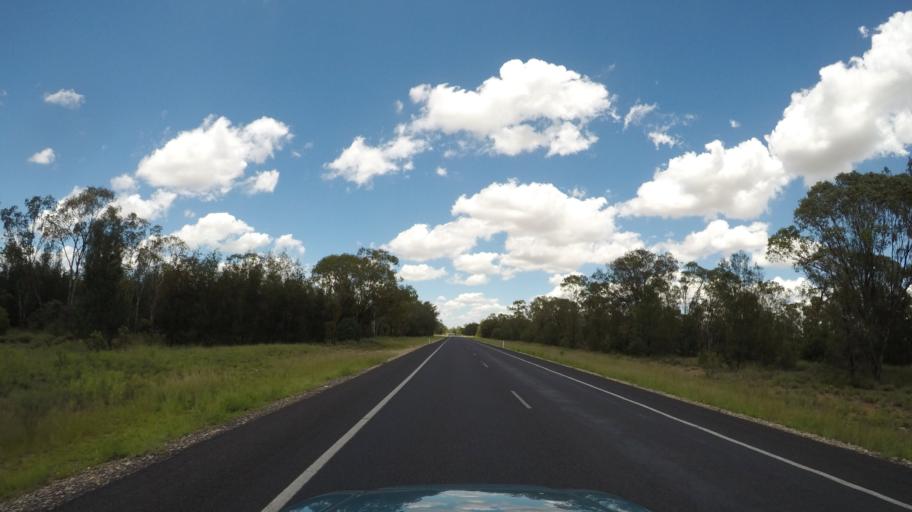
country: AU
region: Queensland
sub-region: Goondiwindi
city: Goondiwindi
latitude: -28.0622
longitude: 150.7634
